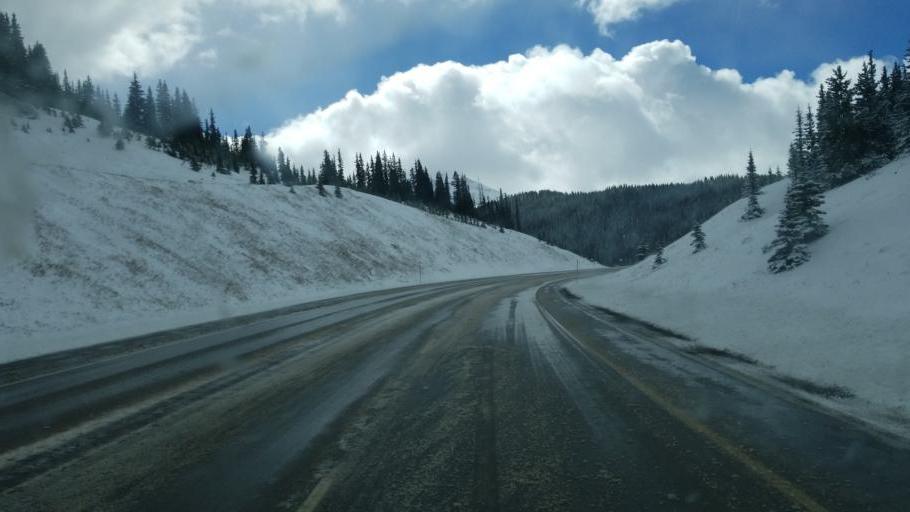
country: US
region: Colorado
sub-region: Summit County
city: Breckenridge
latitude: 39.4186
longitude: -106.1718
